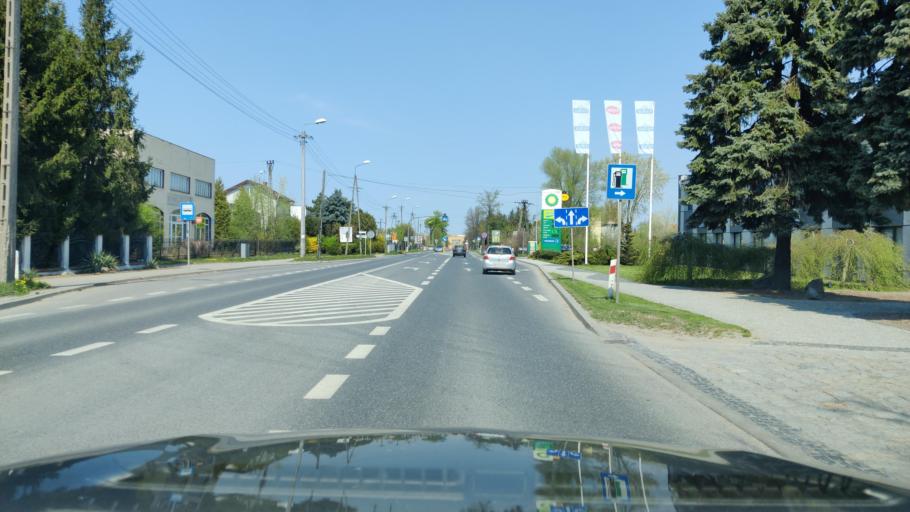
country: PL
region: Masovian Voivodeship
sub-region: Powiat pultuski
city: Pultusk
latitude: 52.6920
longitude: 21.0808
